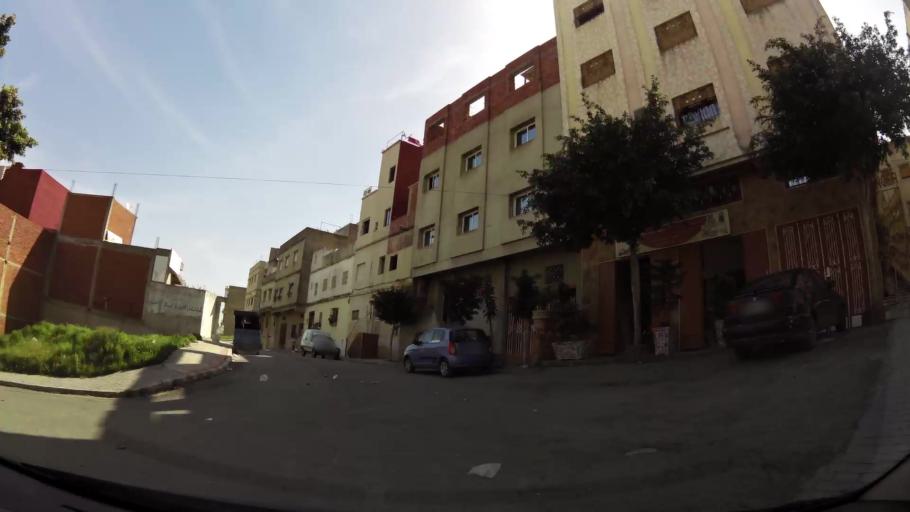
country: MA
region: Tanger-Tetouan
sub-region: Tanger-Assilah
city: Tangier
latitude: 35.7413
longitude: -5.8047
